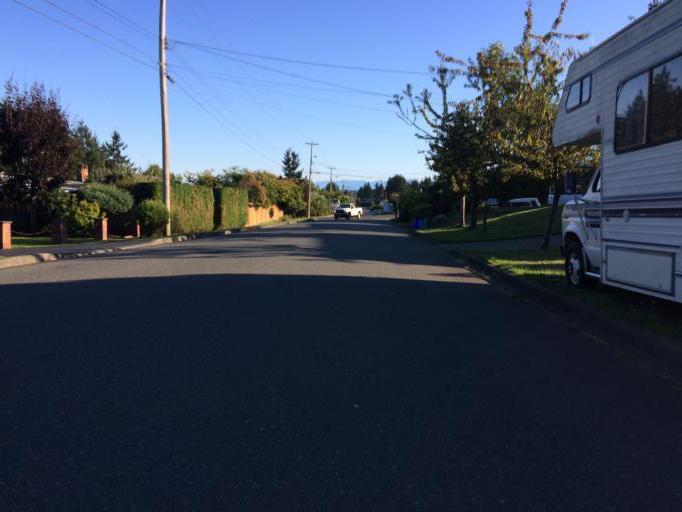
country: CA
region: British Columbia
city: Campbell River
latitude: 49.9931
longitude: -125.2324
